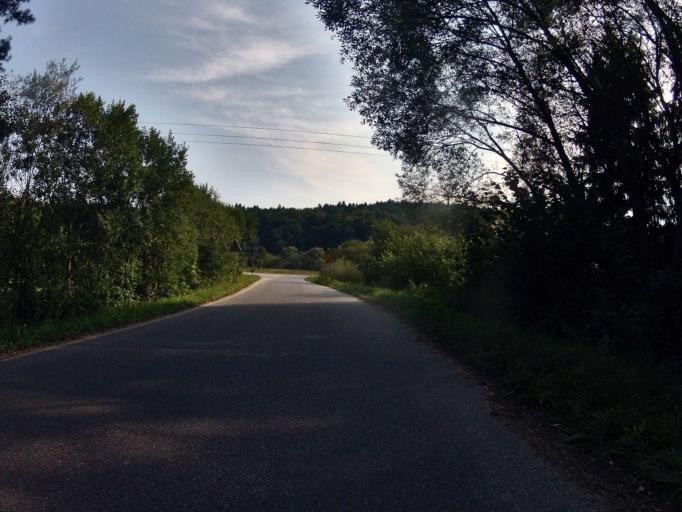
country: PL
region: Subcarpathian Voivodeship
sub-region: Powiat jasielski
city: Krempna
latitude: 49.5055
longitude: 21.5364
